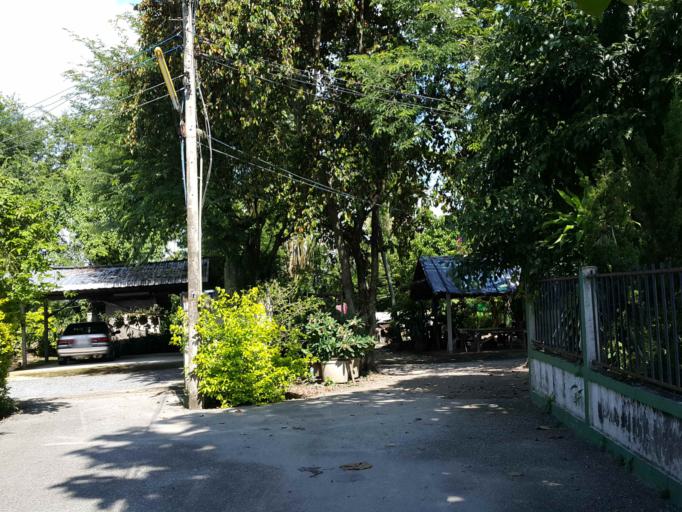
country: TH
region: Chiang Mai
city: San Sai
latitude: 18.8095
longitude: 99.0911
